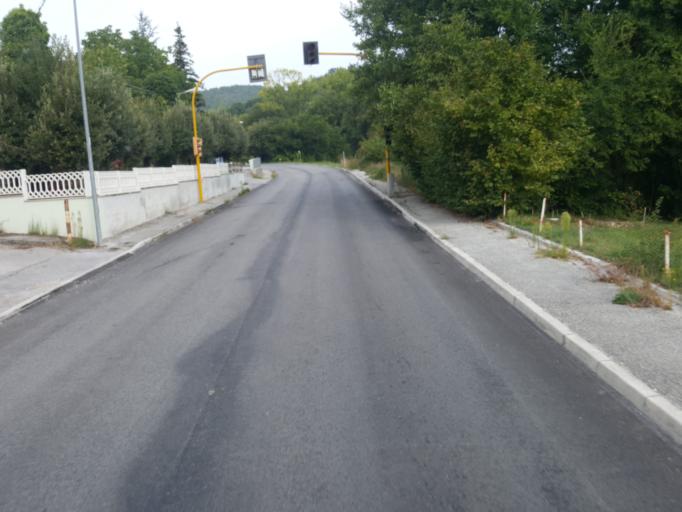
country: IT
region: The Marches
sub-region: Provincia di Ancona
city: Fabriano
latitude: 43.3485
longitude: 12.8380
